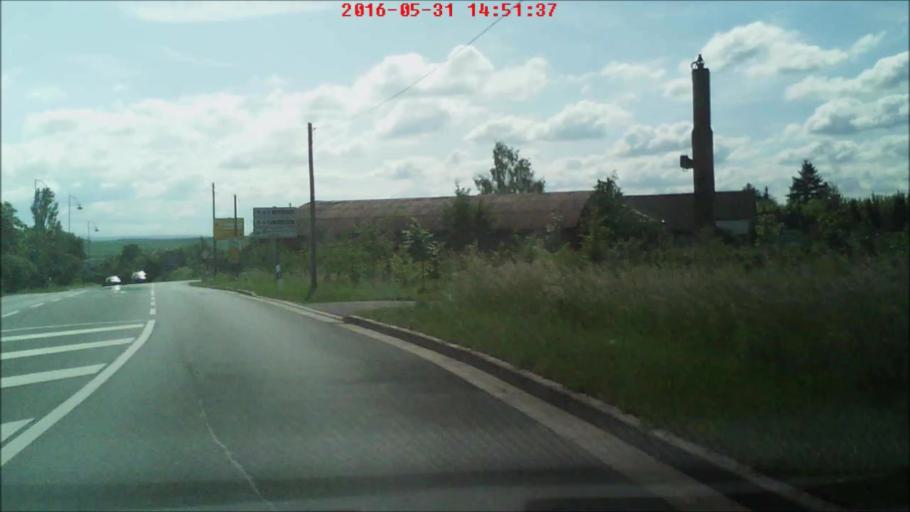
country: DE
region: Thuringia
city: Weissensee
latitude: 51.2052
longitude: 11.0649
